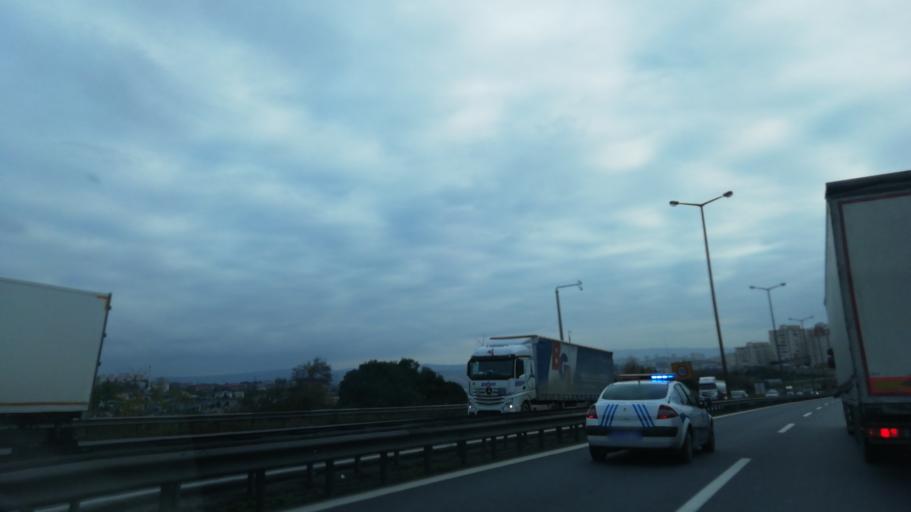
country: TR
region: Kocaeli
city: Izmit
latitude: 40.7834
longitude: 29.9340
